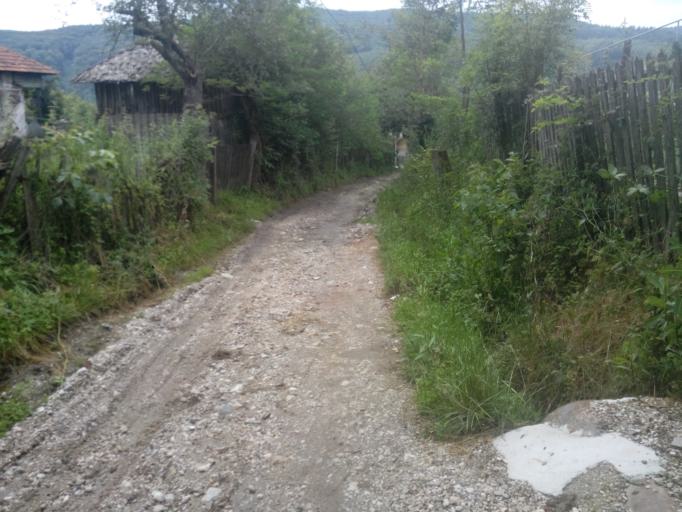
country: RO
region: Arges
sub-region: Comuna Baiculesti
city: Tutana
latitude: 45.0433
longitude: 24.6521
